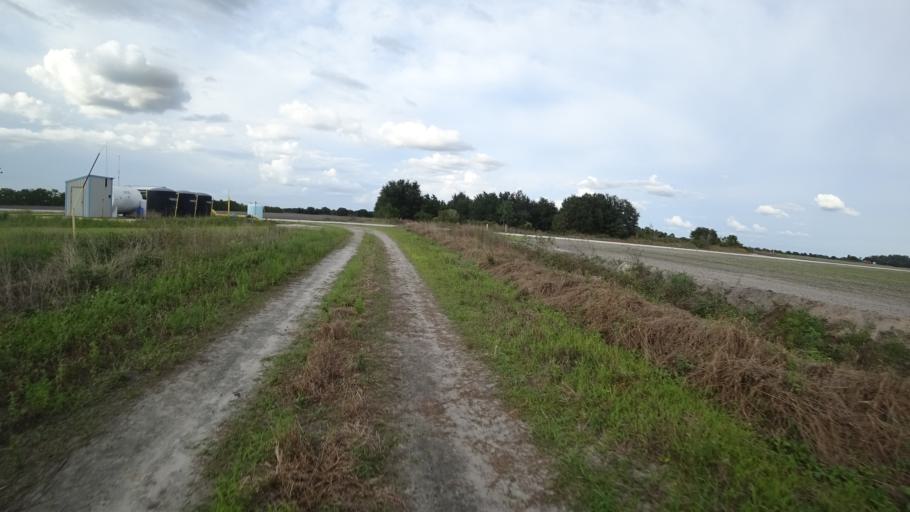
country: US
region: Florida
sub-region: Hillsborough County
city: Wimauma
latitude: 27.5660
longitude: -82.0819
